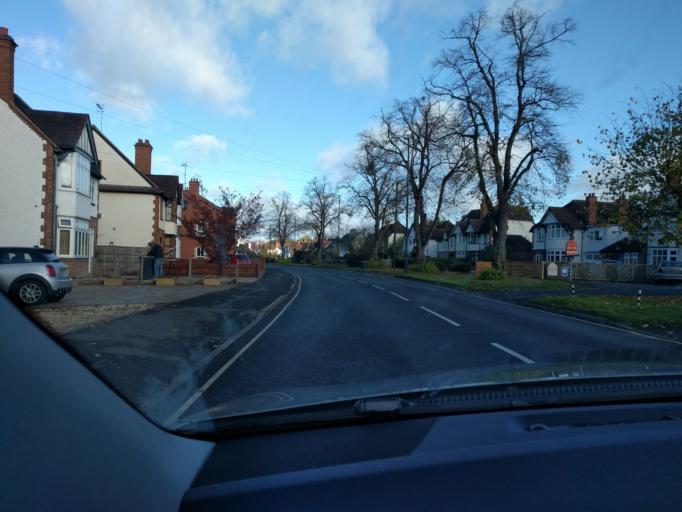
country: GB
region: England
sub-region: Warwickshire
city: Stratford-upon-Avon
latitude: 52.1863
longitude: -1.6994
